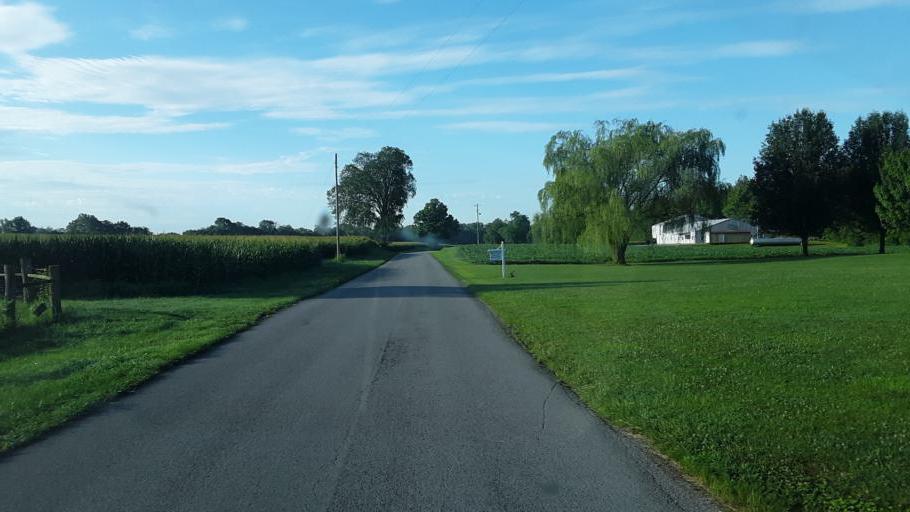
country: US
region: Kentucky
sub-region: Todd County
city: Elkton
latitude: 36.7360
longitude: -87.1678
